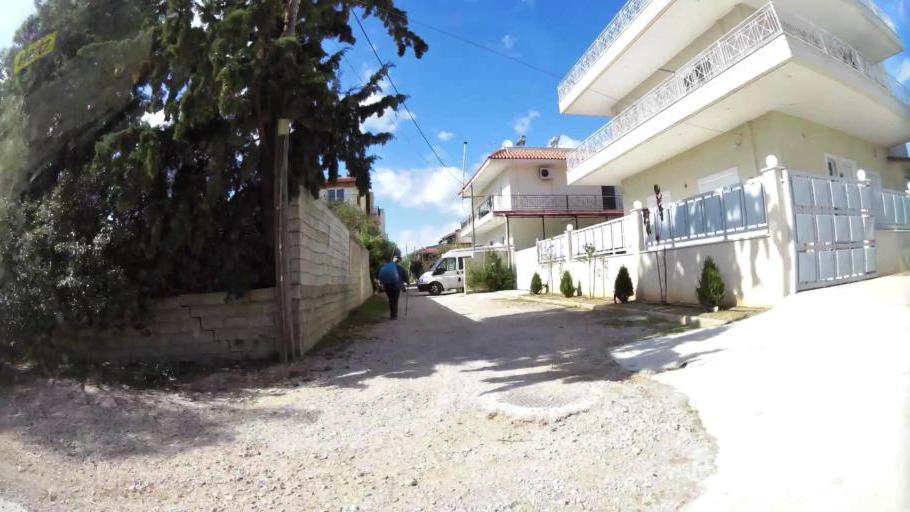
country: GR
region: Attica
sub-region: Nomarchia Anatolikis Attikis
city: Acharnes
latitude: 38.1026
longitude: 23.7469
